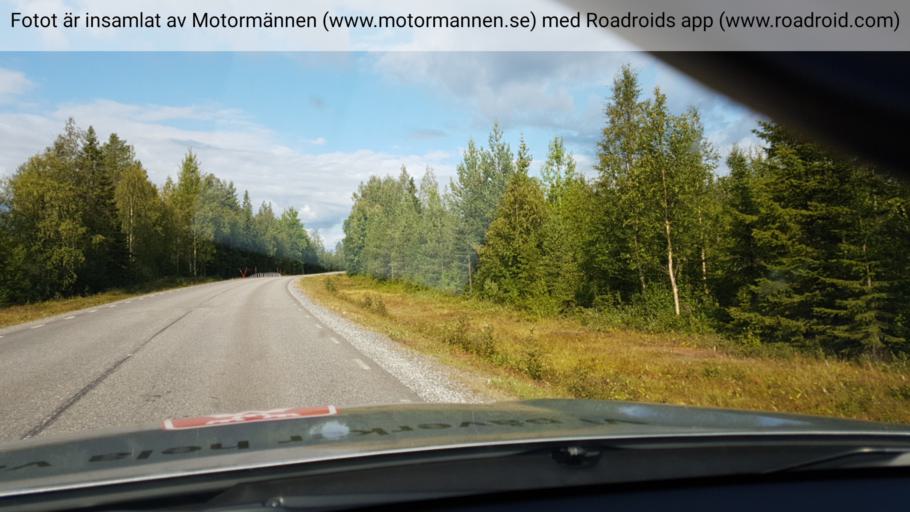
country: SE
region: Vaesterbotten
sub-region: Skelleftea Kommun
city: Storvik
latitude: 65.3379
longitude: 20.5336
